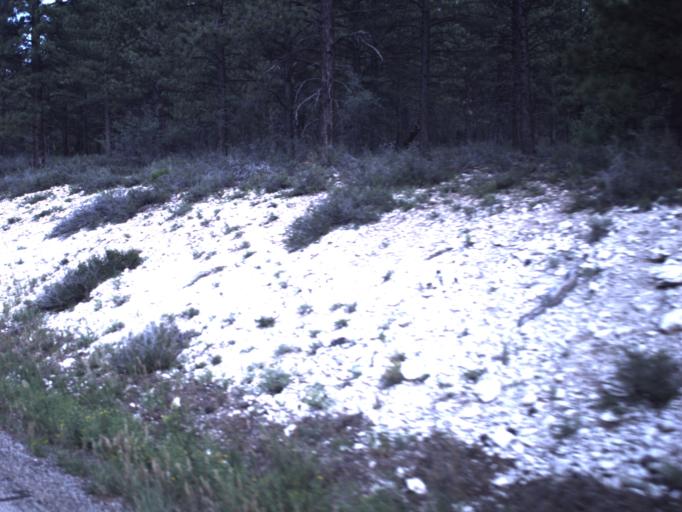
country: US
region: Utah
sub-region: Garfield County
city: Panguitch
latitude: 37.4912
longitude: -112.5654
